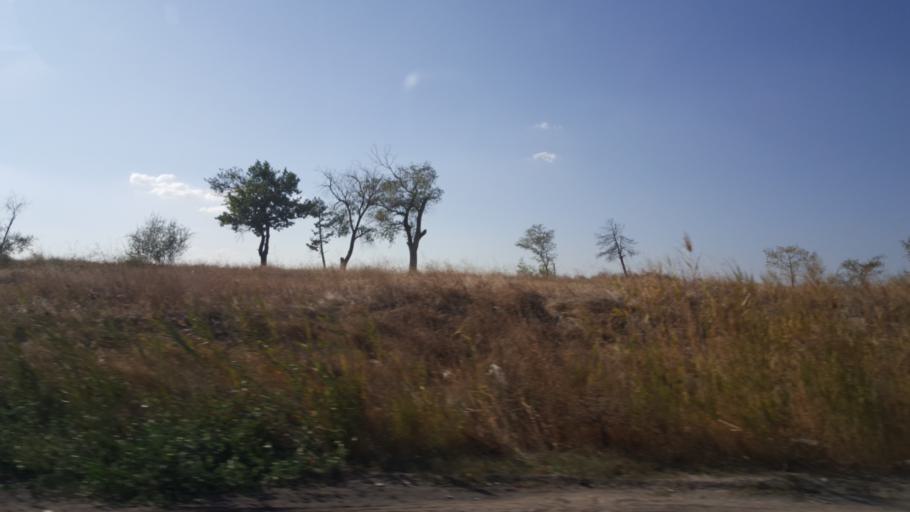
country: TR
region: Ankara
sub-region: Goelbasi
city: Golbasi
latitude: 39.7809
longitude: 32.8042
